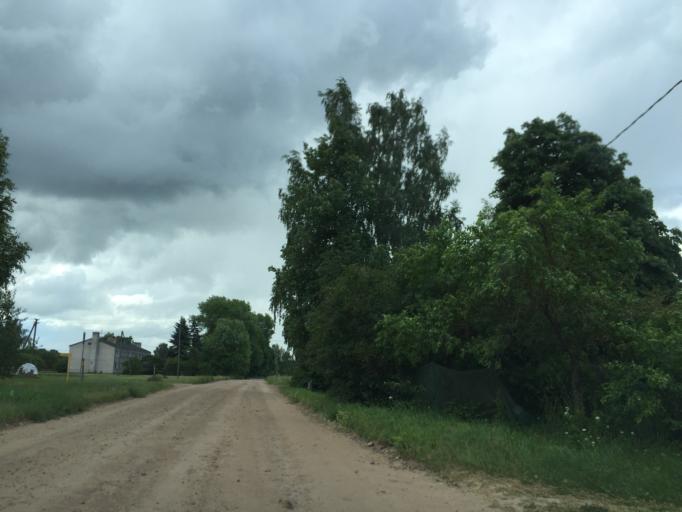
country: LV
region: Lecava
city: Iecava
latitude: 56.6076
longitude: 24.1815
